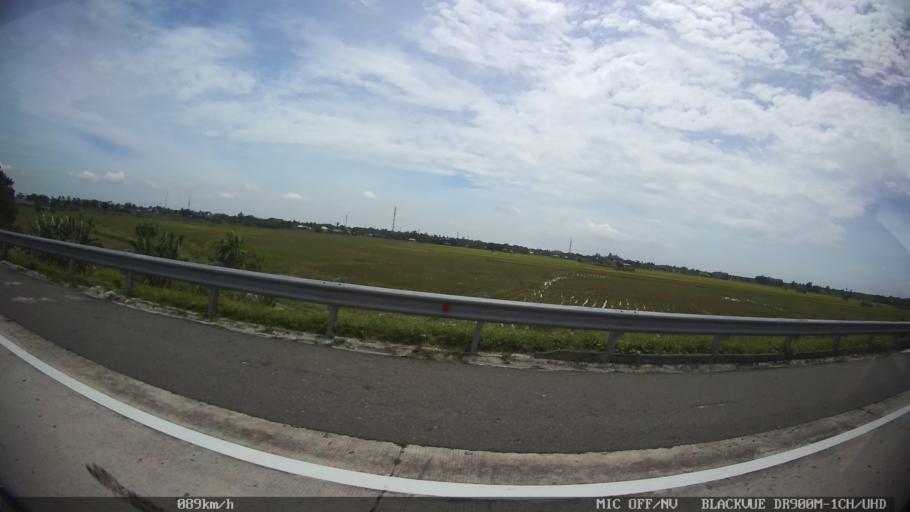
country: ID
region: North Sumatra
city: Percut
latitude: 3.5464
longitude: 98.8535
